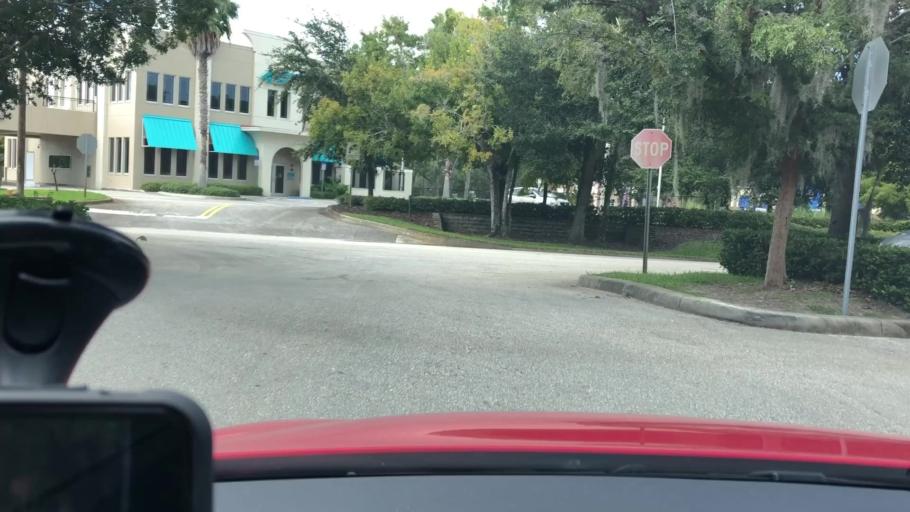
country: US
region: Florida
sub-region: Volusia County
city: Ormond Beach
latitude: 29.2657
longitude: -81.1028
